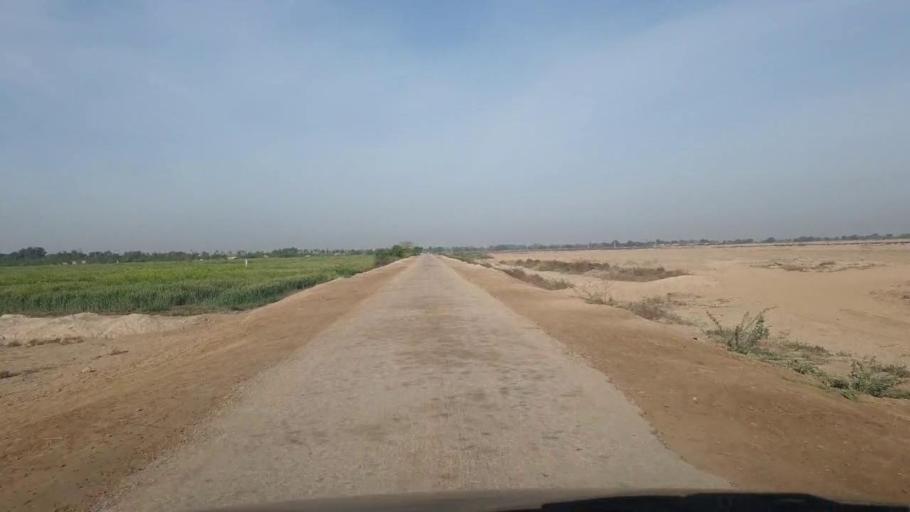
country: PK
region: Sindh
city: Umarkot
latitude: 25.3324
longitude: 69.7096
